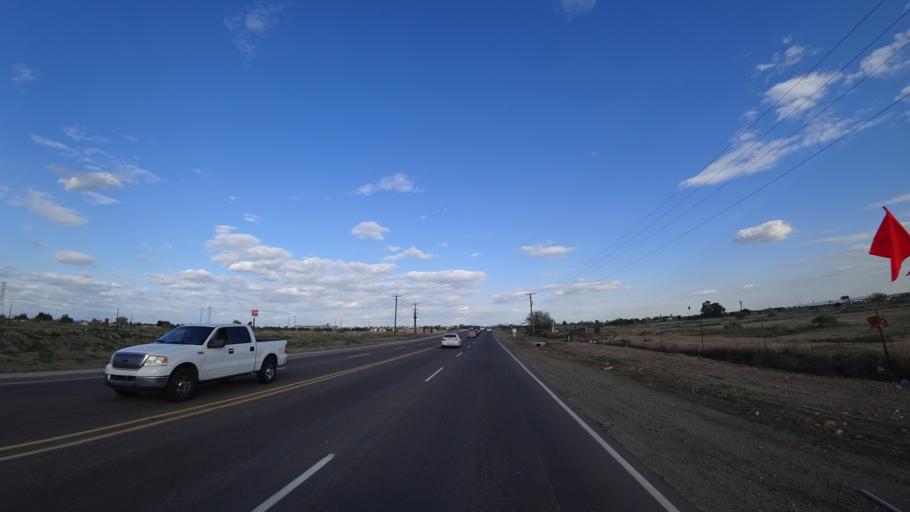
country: US
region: Arizona
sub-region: Maricopa County
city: Sun City
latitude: 33.5512
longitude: -112.2782
